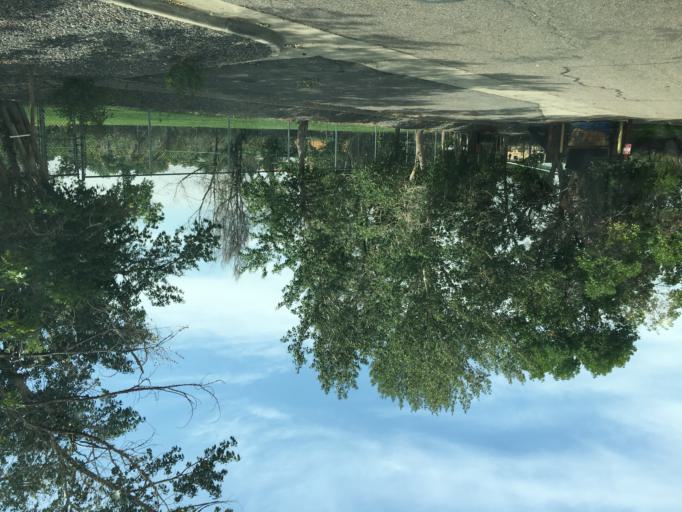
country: US
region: Colorado
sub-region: Adams County
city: Aurora
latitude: 39.7351
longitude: -104.8055
